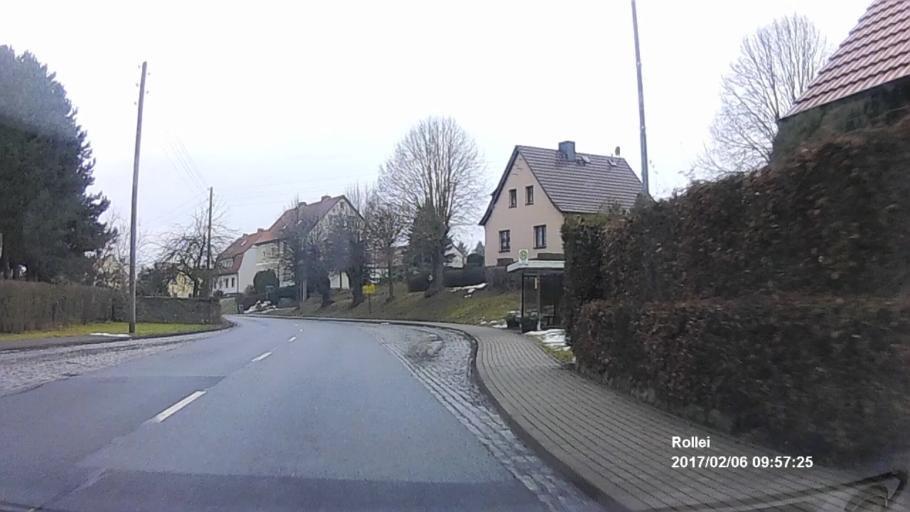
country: DE
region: Thuringia
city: Niedersachswerfen
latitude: 51.5046
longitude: 10.7211
